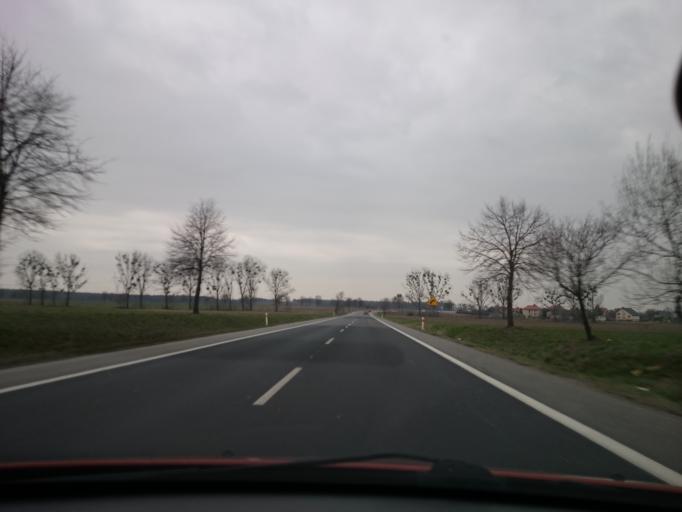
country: PL
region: Opole Voivodeship
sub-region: Powiat nyski
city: Lambinowice
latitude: 50.5978
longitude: 17.5352
